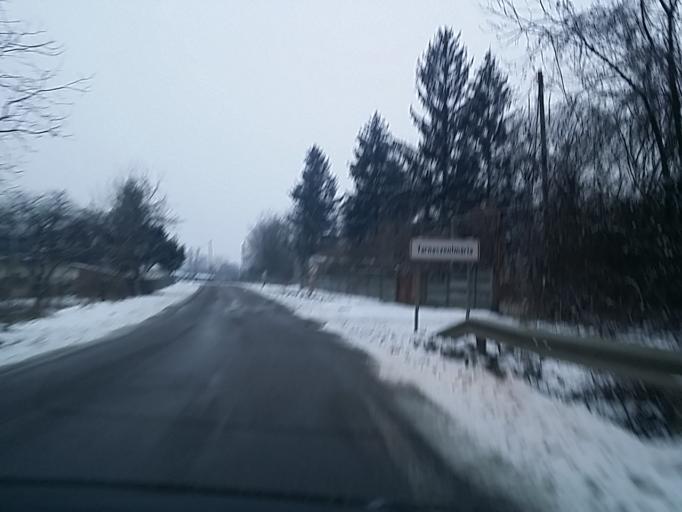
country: HU
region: Heves
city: Verpelet
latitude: 47.8796
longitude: 20.1961
